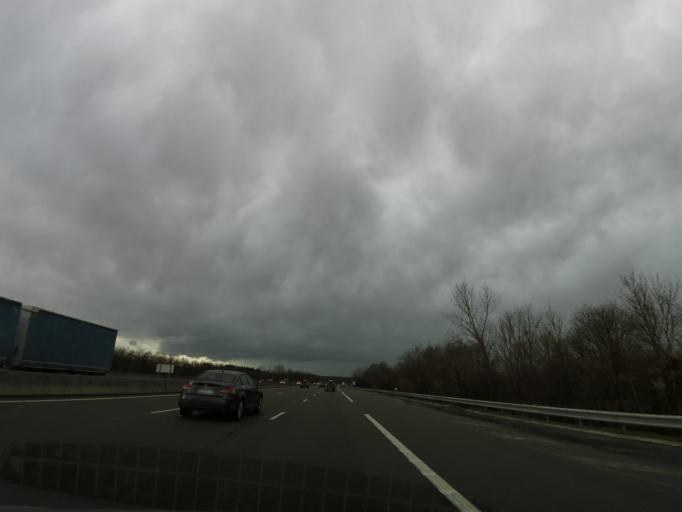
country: FR
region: Rhone-Alpes
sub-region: Departement de l'Ain
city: Saint-Martin-du-Mont
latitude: 46.0764
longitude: 5.3045
